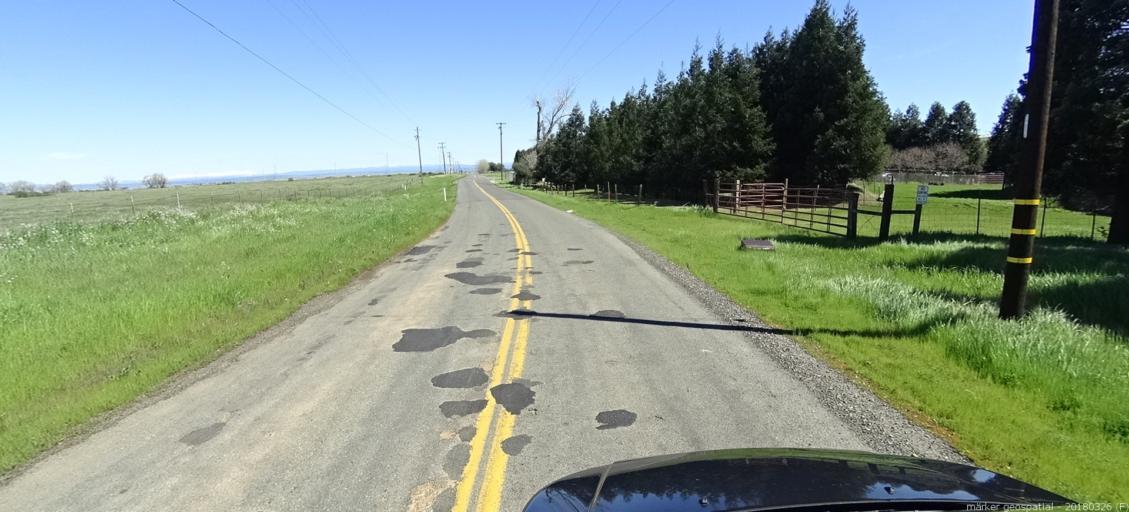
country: US
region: California
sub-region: Sacramento County
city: Rancho Cordova
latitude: 38.5256
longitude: -121.2521
